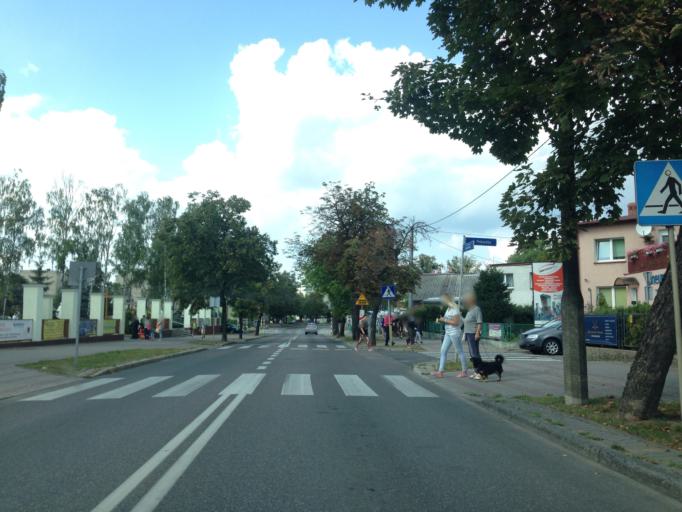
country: PL
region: Warmian-Masurian Voivodeship
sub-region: Powiat ilawski
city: Ilawa
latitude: 53.5915
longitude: 19.5691
